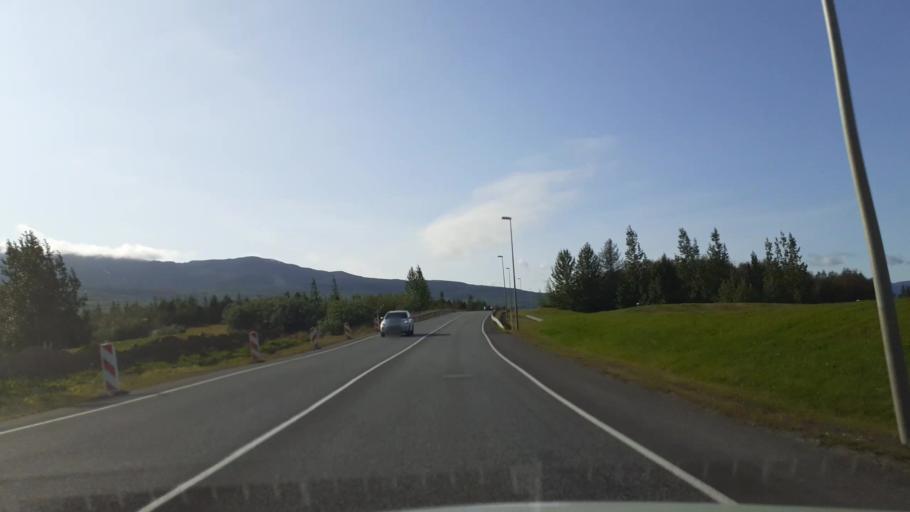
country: IS
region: Northeast
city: Akureyri
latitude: 65.6724
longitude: -18.1218
